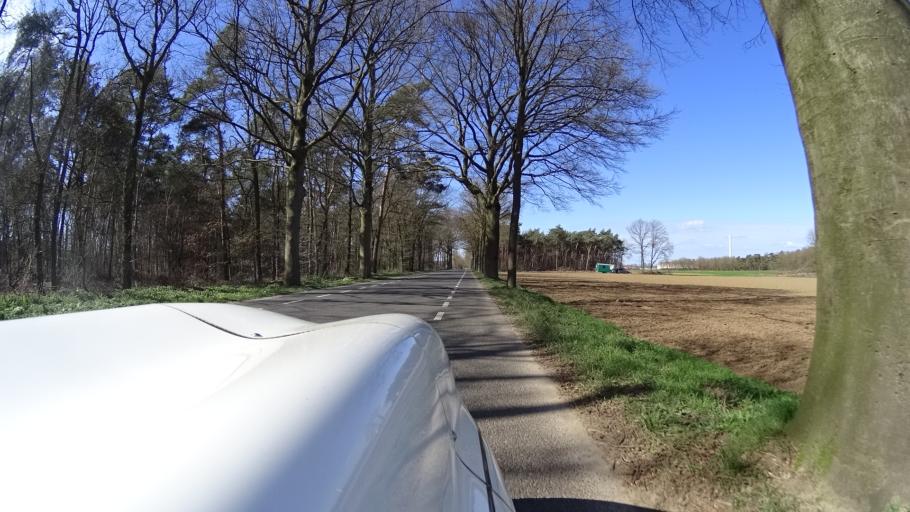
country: NL
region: Limburg
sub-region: Gemeente Bergen
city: Wellerlooi
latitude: 51.5165
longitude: 6.1294
